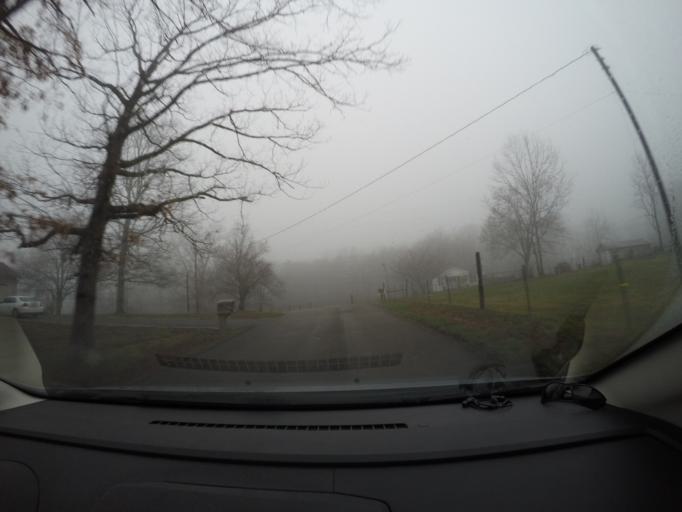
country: US
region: Tennessee
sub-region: Marion County
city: Powells Crossroads
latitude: 35.1711
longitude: -85.4241
